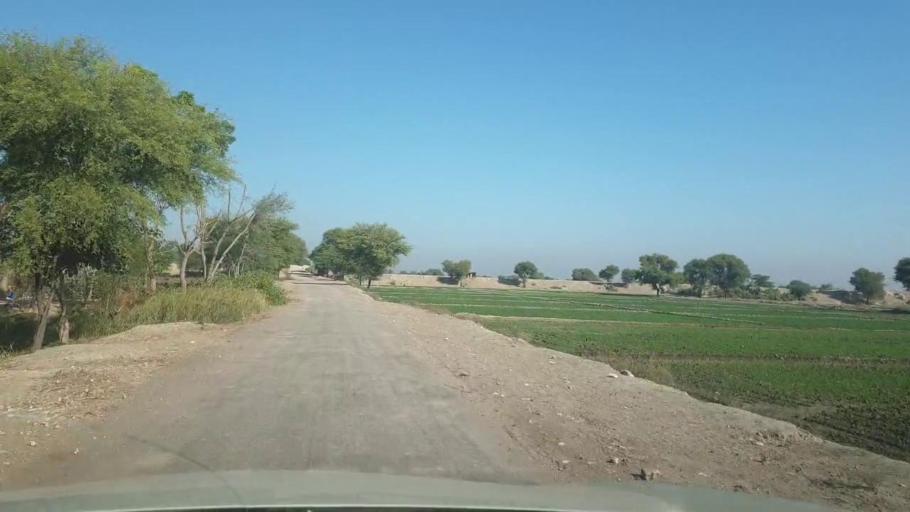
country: PK
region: Sindh
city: Bhan
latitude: 26.5563
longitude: 67.6641
